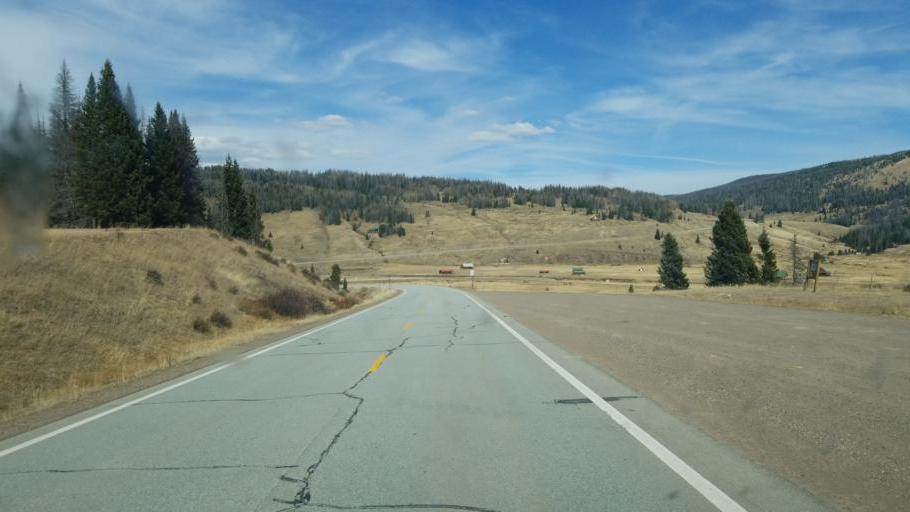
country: US
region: New Mexico
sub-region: Rio Arriba County
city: Chama
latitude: 37.0385
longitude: -106.4111
